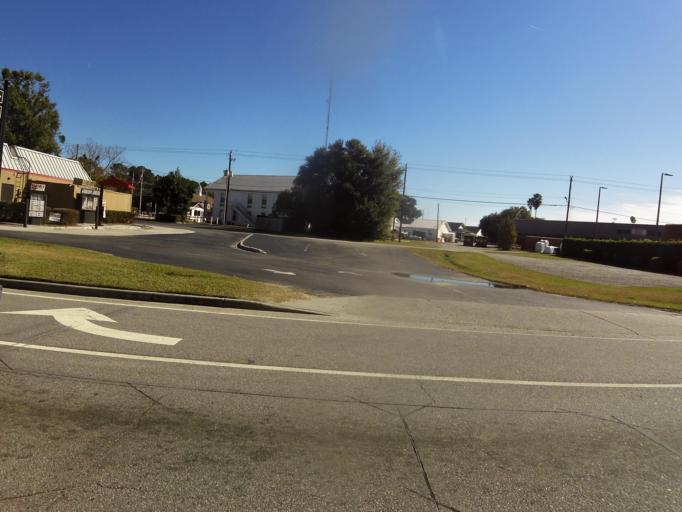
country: US
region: Georgia
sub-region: Bryan County
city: Richmond Hill
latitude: 31.9492
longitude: -81.3128
